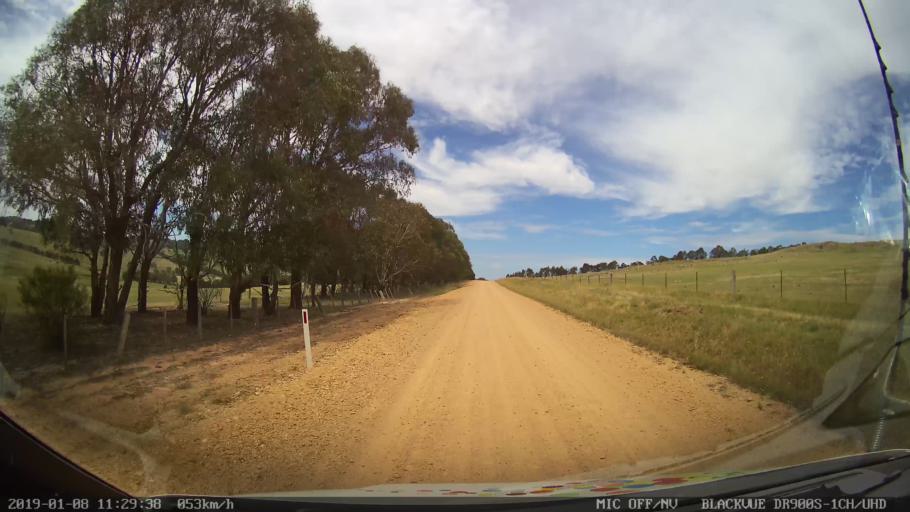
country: AU
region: New South Wales
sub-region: Guyra
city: Guyra
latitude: -30.3018
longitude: 151.5479
